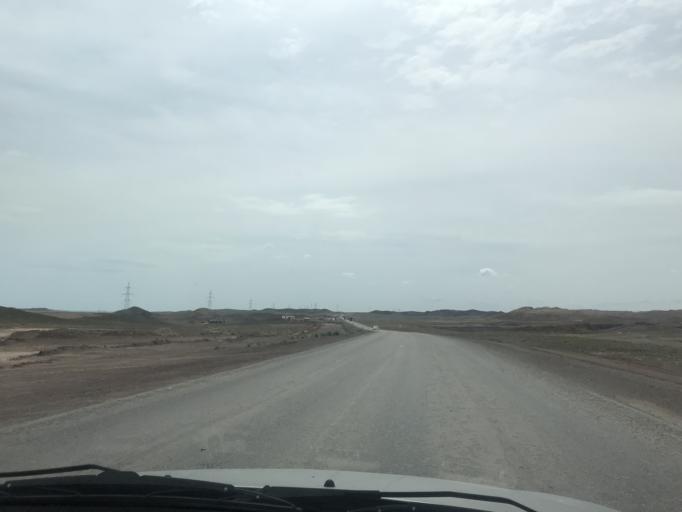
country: KZ
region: Zhambyl
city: Mynaral
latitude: 45.3683
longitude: 73.6606
